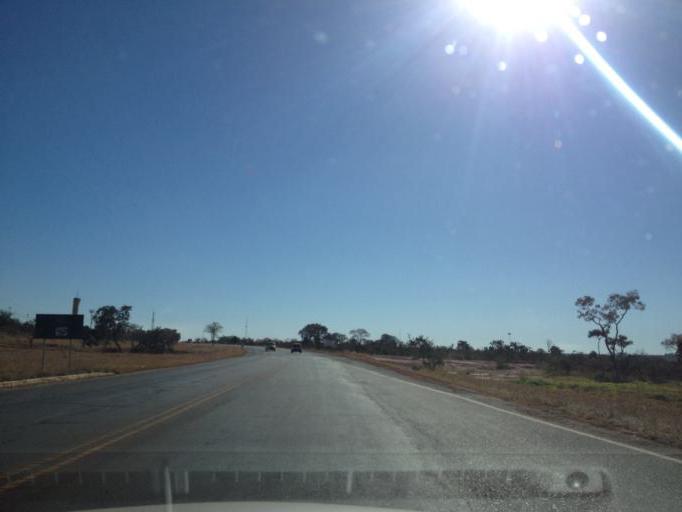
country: BR
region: Federal District
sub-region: Brasilia
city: Brasilia
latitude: -15.6932
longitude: -47.8363
